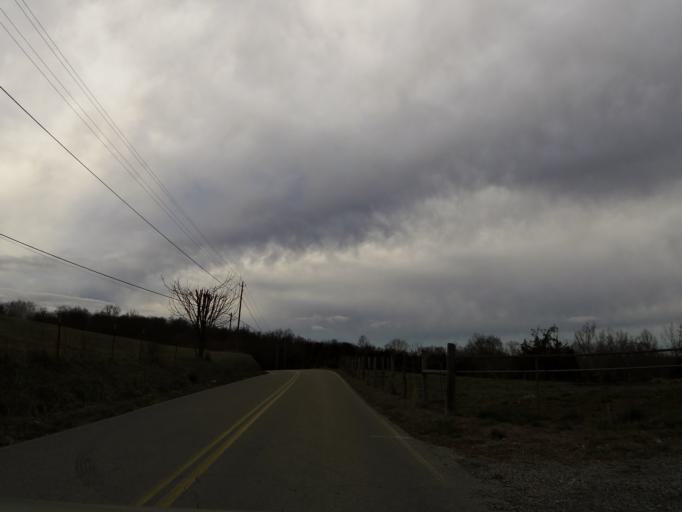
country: US
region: Tennessee
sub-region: Greene County
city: Tusculum
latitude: 36.2079
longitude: -82.7466
